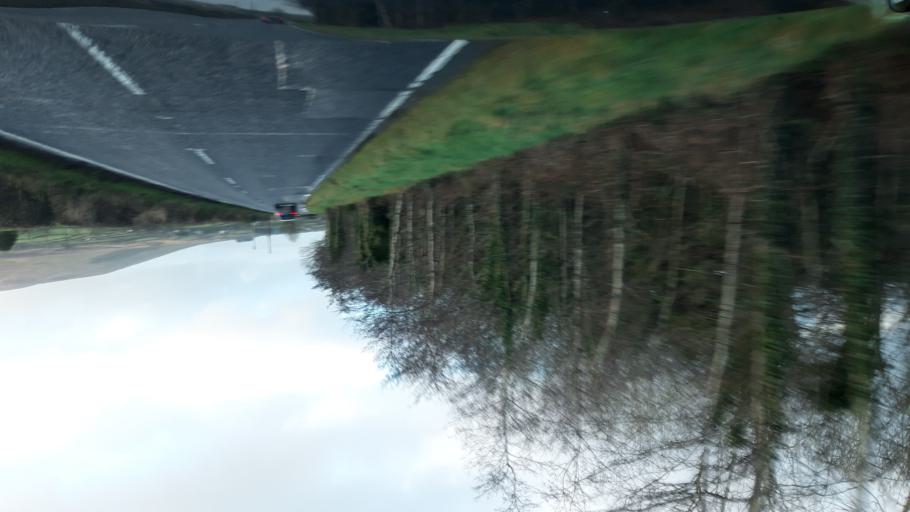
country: GB
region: Northern Ireland
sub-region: Moyle District
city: Ballycastle
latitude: 55.1412
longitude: -6.3213
